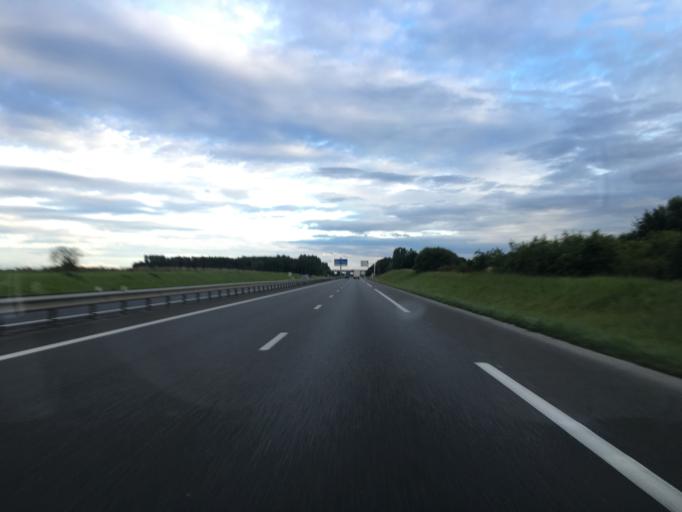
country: FR
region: Ile-de-France
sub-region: Departement de Seine-et-Marne
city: Moissy-Cramayel
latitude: 48.6188
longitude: 2.6305
